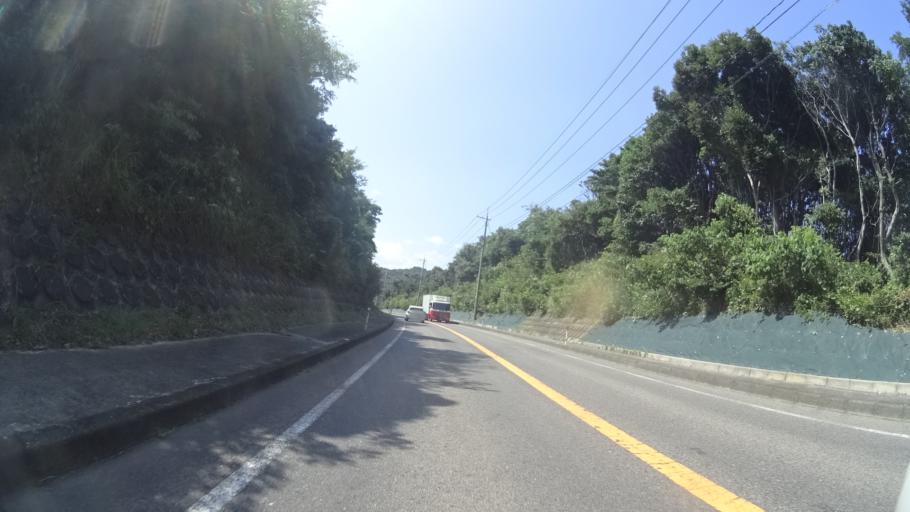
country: JP
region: Shimane
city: Masuda
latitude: 34.6742
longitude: 131.7183
